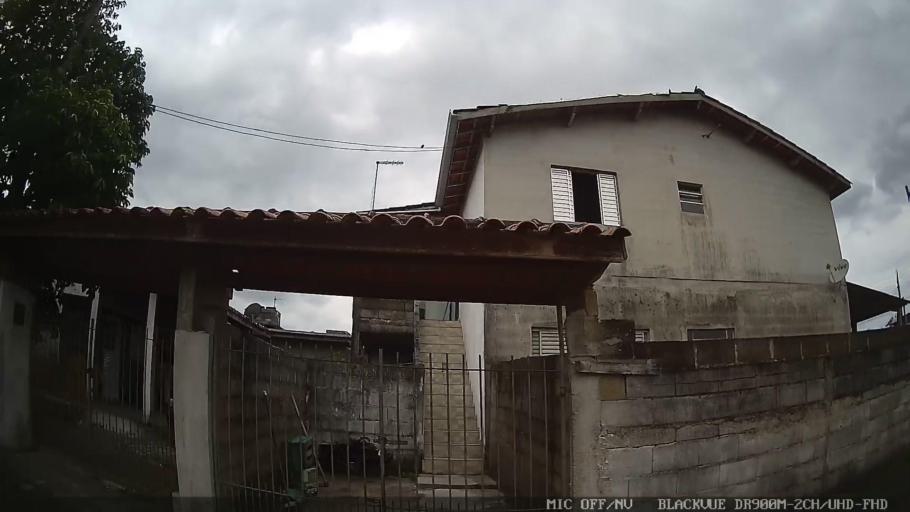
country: BR
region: Sao Paulo
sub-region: Caraguatatuba
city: Caraguatatuba
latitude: -23.6784
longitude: -45.4507
